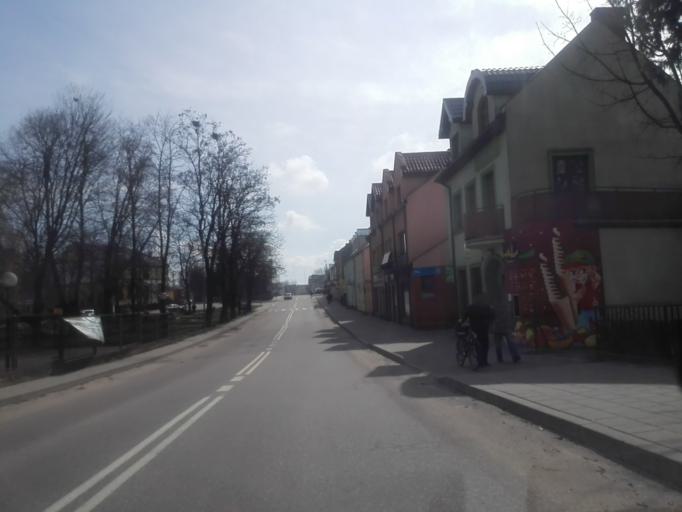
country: PL
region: Podlasie
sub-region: Powiat sejnenski
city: Sejny
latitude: 54.1081
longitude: 23.3468
